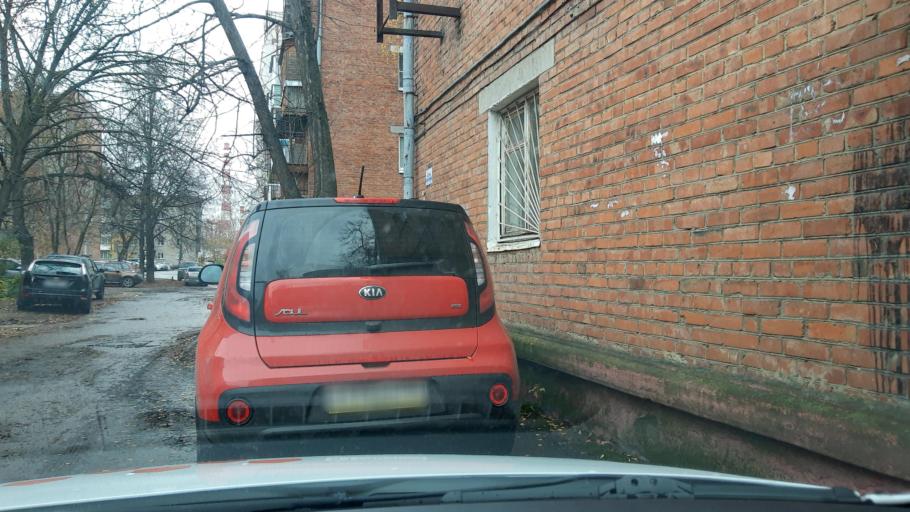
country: RU
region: Moskovskaya
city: Elektrostal'
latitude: 55.7781
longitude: 38.4503
